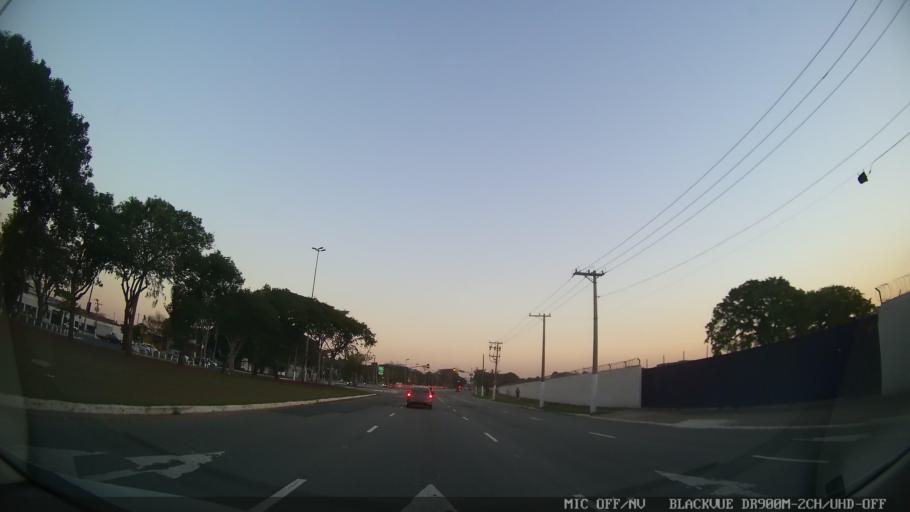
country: BR
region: Sao Paulo
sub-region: Sao Paulo
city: Sao Paulo
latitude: -23.5087
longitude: -46.6295
